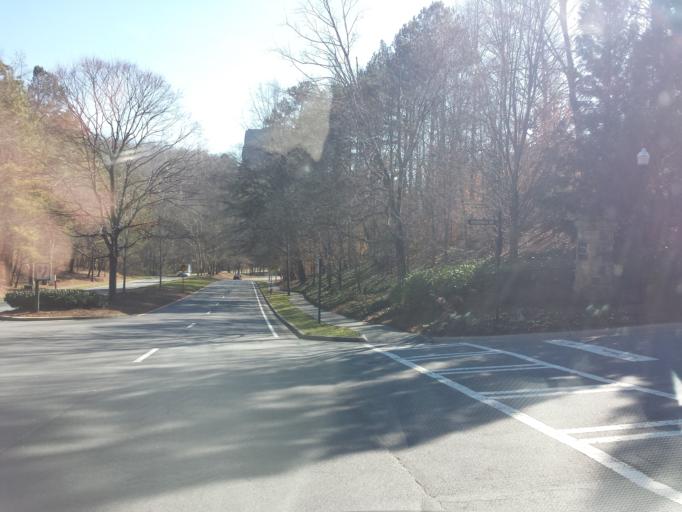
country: US
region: Georgia
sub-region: Cobb County
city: Vinings
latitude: 33.9102
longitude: -84.4600
